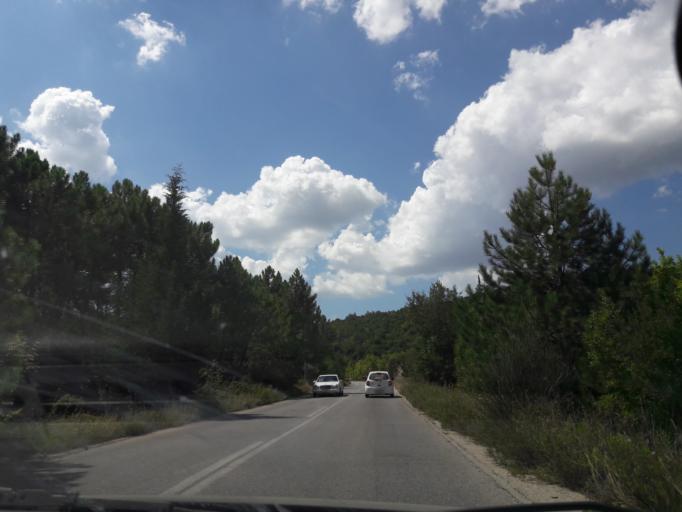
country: GR
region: Central Macedonia
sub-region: Nomos Chalkidikis
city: Polygyros
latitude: 40.3624
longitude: 23.4954
